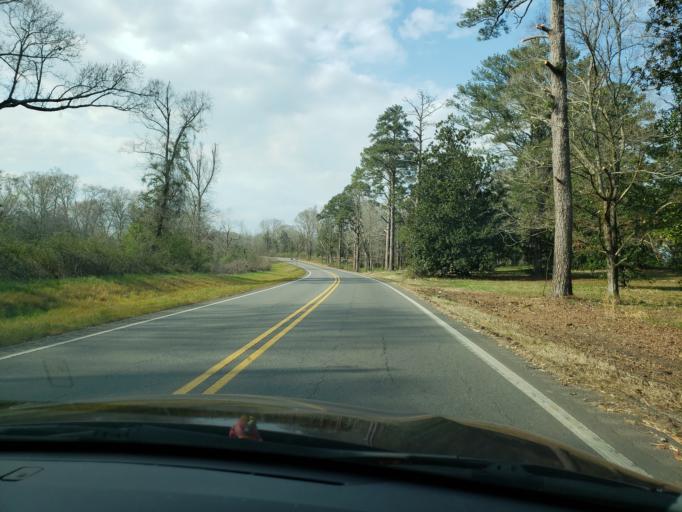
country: US
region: Alabama
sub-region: Hale County
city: Greensboro
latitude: 32.7059
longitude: -87.6073
